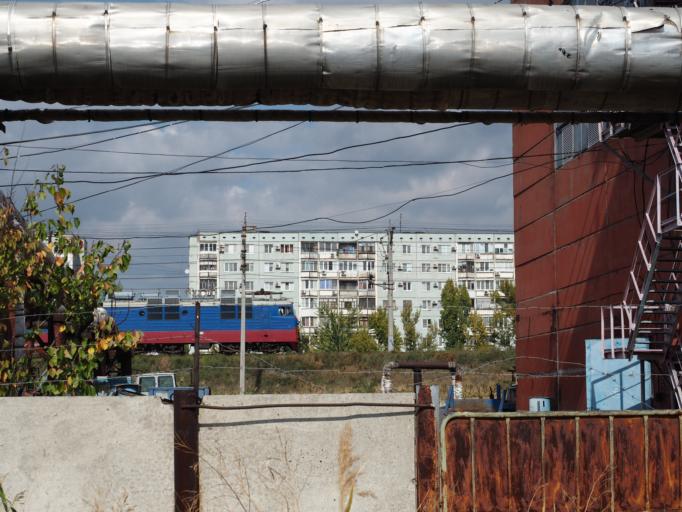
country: RU
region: Volgograd
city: Krasnoslobodsk
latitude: 48.5059
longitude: 44.5460
